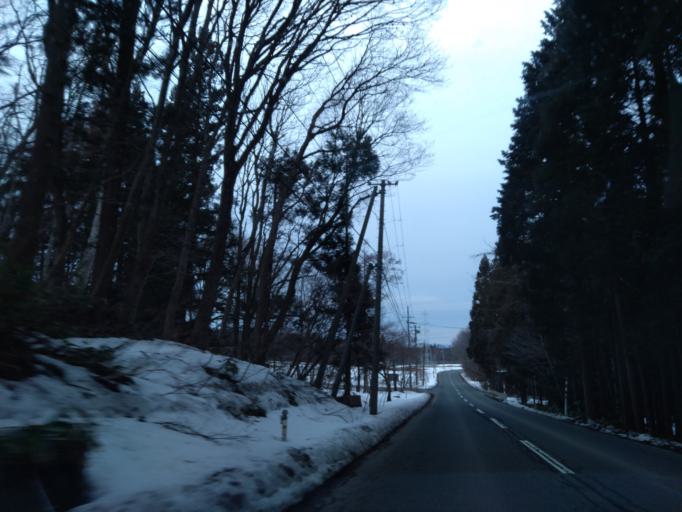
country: JP
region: Iwate
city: Kitakami
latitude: 39.2406
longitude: 140.9793
